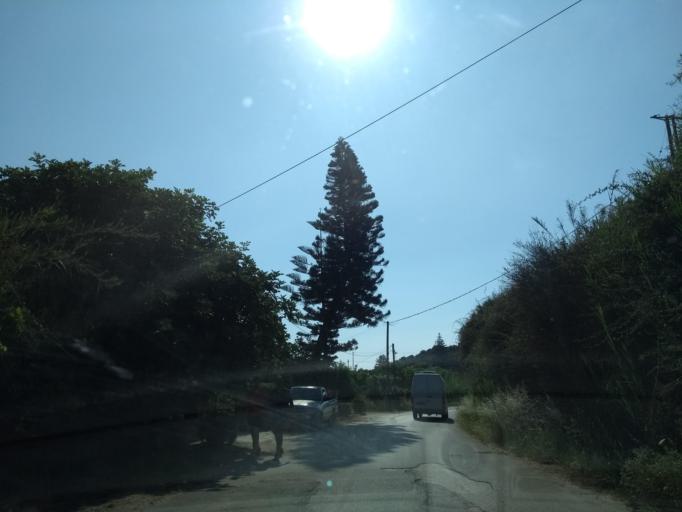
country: GR
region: Crete
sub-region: Nomos Chanias
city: Georgioupolis
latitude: 35.3584
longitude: 24.2624
